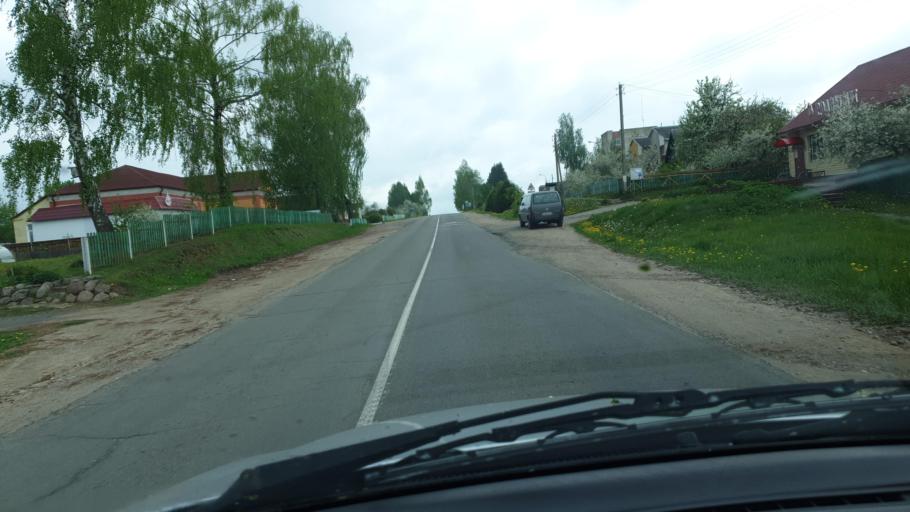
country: BY
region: Vitebsk
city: Lyepyel'
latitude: 54.8876
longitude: 28.6246
